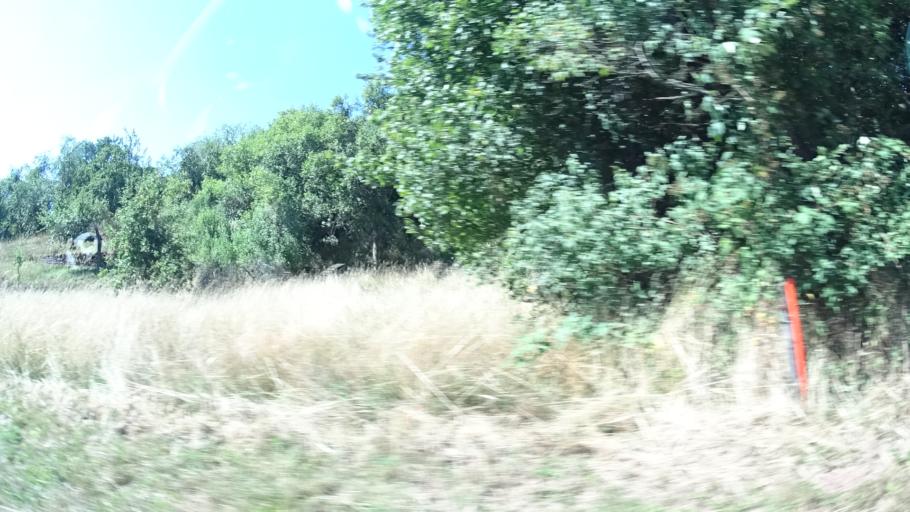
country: DE
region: Baden-Wuerttemberg
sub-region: Regierungsbezirk Stuttgart
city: Wertheim
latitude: 49.7438
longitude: 9.5163
